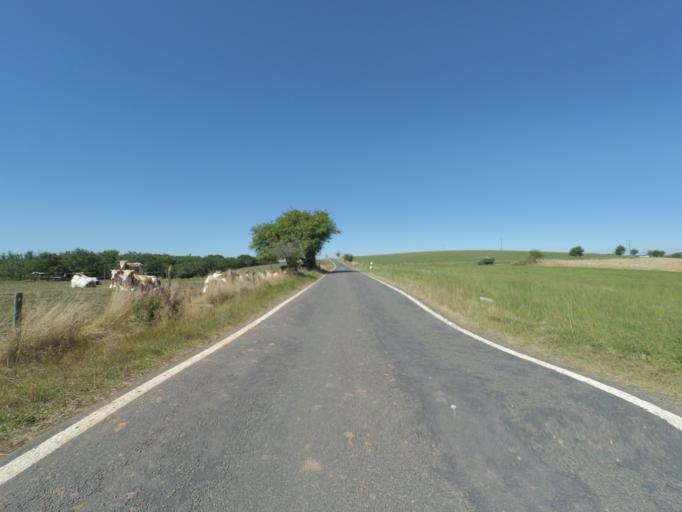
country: DE
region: Rheinland-Pfalz
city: Bad Bertrich
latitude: 50.0575
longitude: 7.0286
